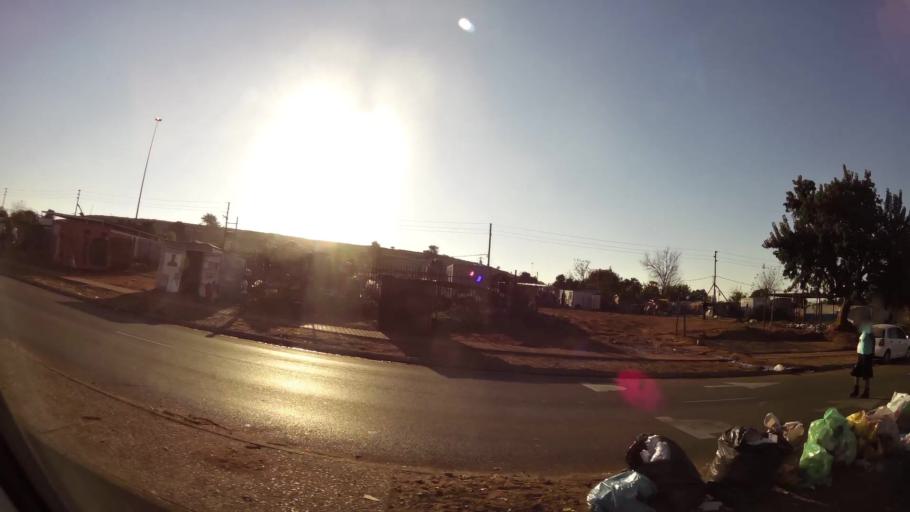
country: ZA
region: Gauteng
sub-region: City of Tshwane Metropolitan Municipality
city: Cullinan
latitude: -25.7012
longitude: 28.3962
